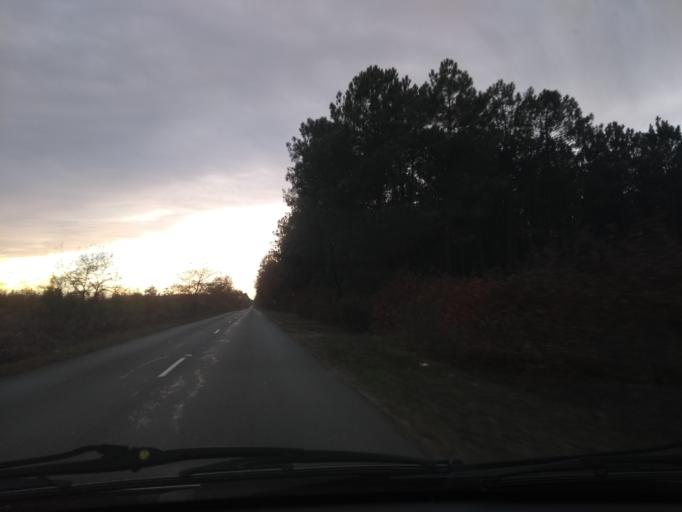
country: FR
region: Aquitaine
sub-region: Departement de la Gironde
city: Saucats
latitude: 44.6470
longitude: -0.6169
